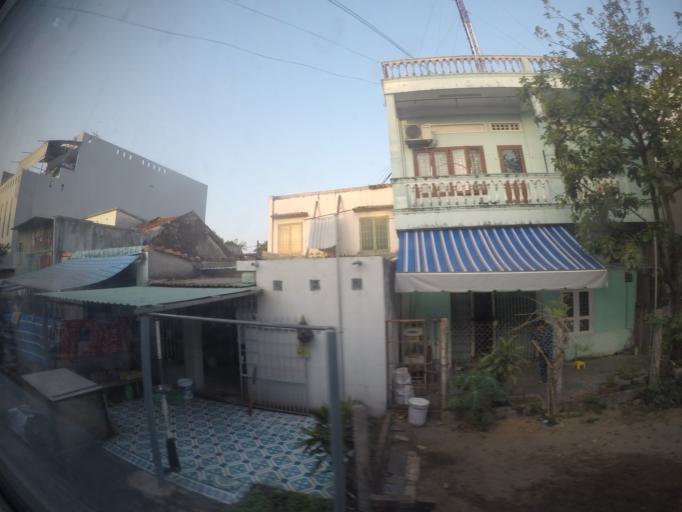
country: VN
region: Phu Yen
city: Tuy Hoa
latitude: 13.0963
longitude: 109.2932
